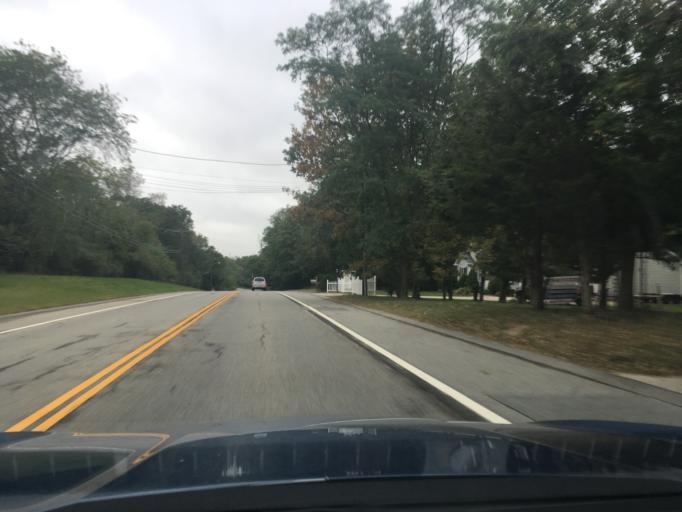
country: US
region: Rhode Island
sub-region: Kent County
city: East Greenwich
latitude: 41.6219
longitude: -71.4802
